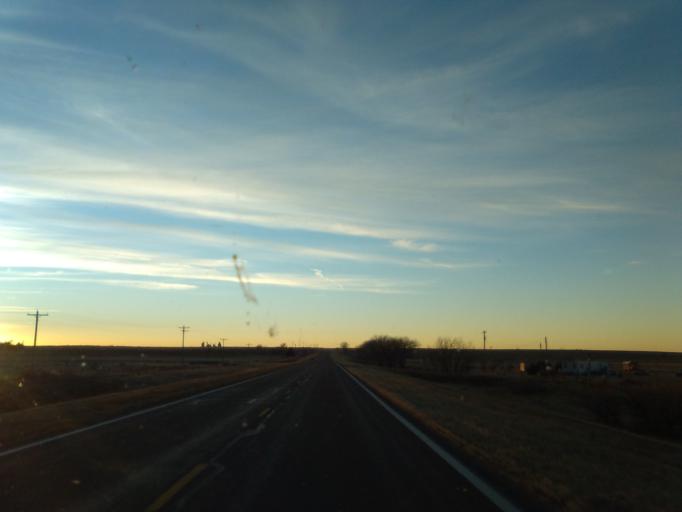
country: US
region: Kansas
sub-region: Wallace County
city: Sharon Springs
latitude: 38.9022
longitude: -101.6976
